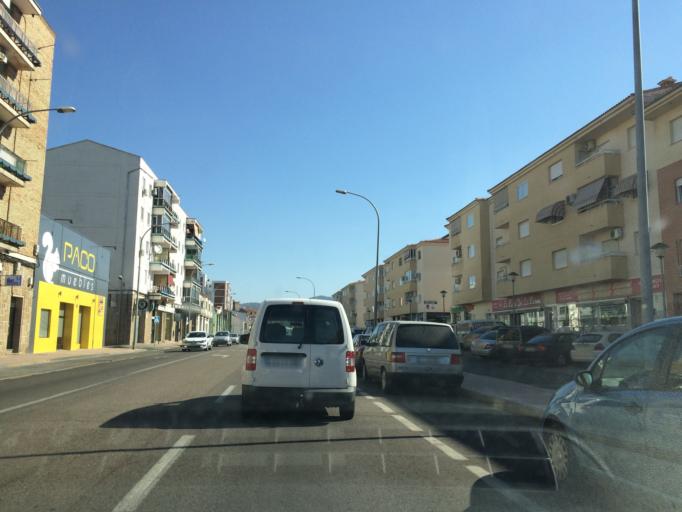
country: ES
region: Extremadura
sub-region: Provincia de Caceres
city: Plasencia
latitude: 40.0230
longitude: -6.0967
